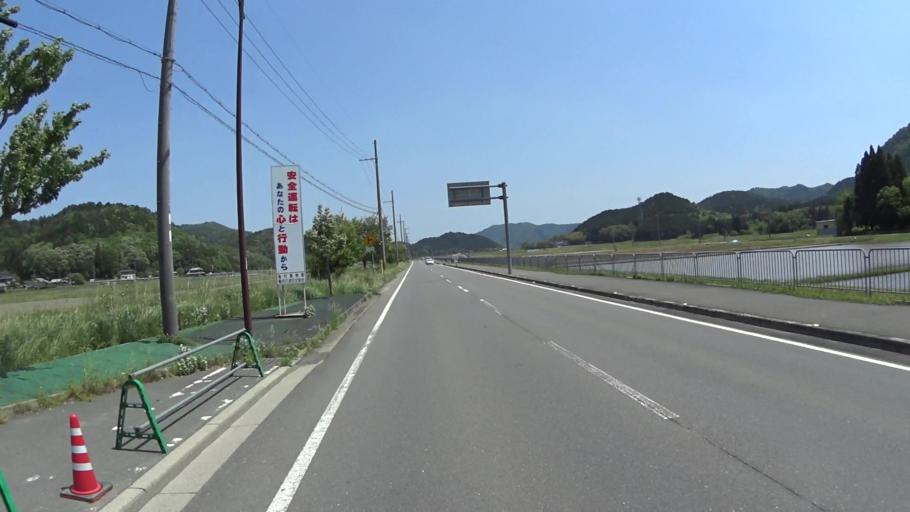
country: JP
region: Kyoto
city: Kameoka
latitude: 35.0513
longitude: 135.4737
